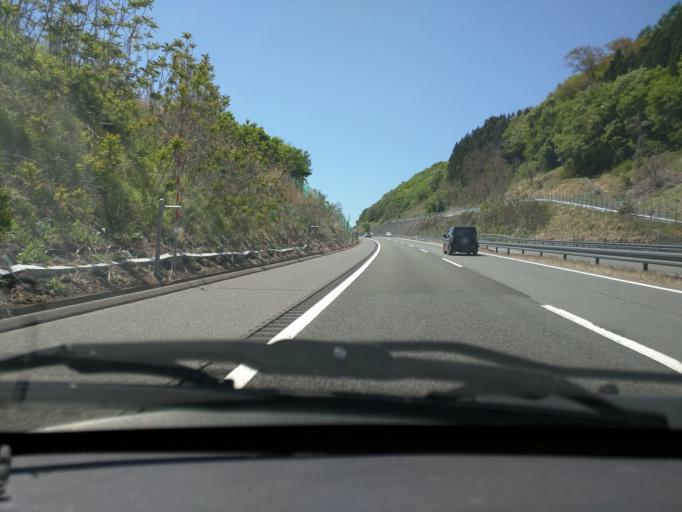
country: JP
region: Nagano
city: Nakano
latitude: 36.7666
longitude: 138.3165
